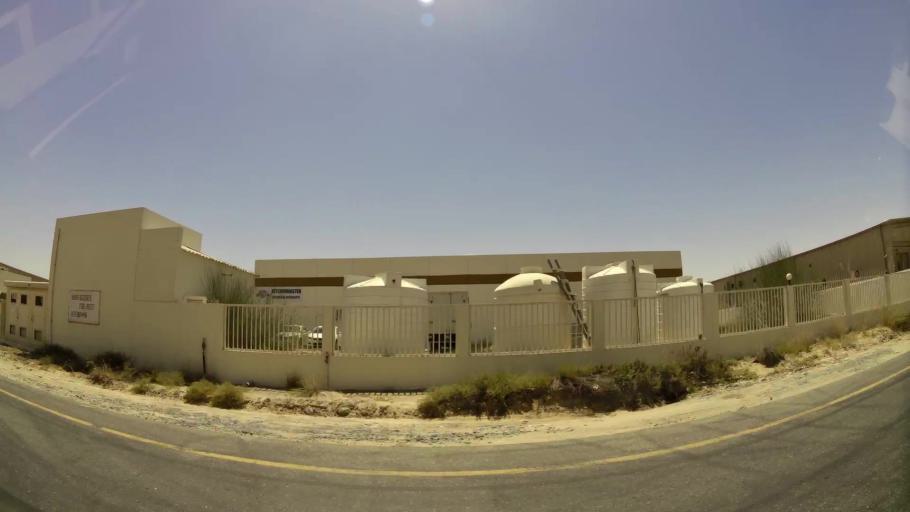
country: AE
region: Dubai
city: Dubai
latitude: 24.9777
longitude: 55.1867
